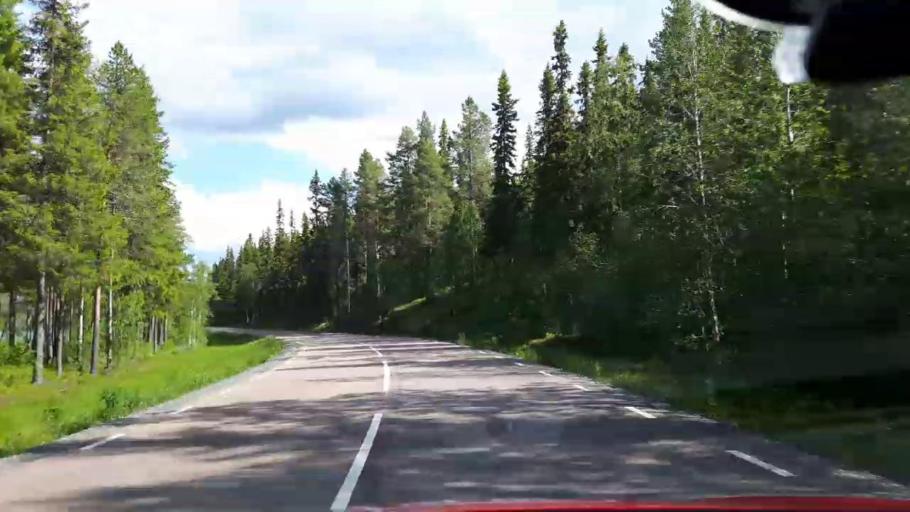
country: SE
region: Jaemtland
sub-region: Krokoms Kommun
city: Valla
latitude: 63.9585
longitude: 14.1905
